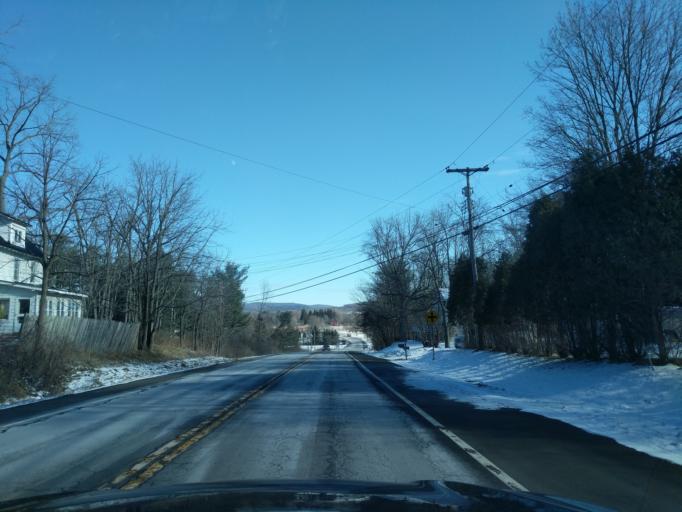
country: US
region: New York
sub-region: Tompkins County
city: East Ithaca
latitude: 42.3950
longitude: -76.3786
